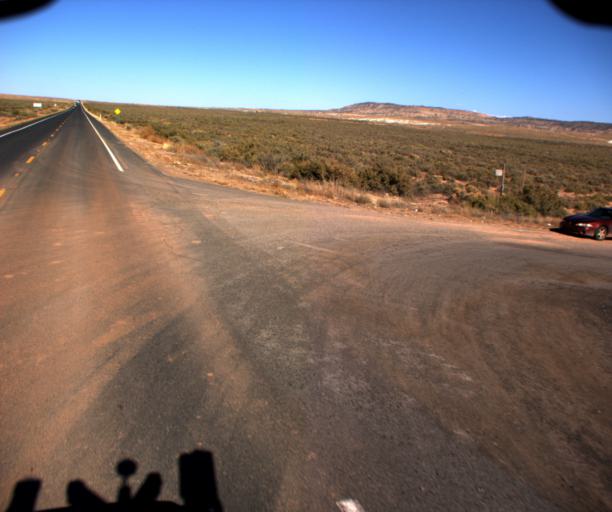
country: US
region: Arizona
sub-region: Coconino County
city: Kaibito
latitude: 36.3329
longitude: -110.9231
